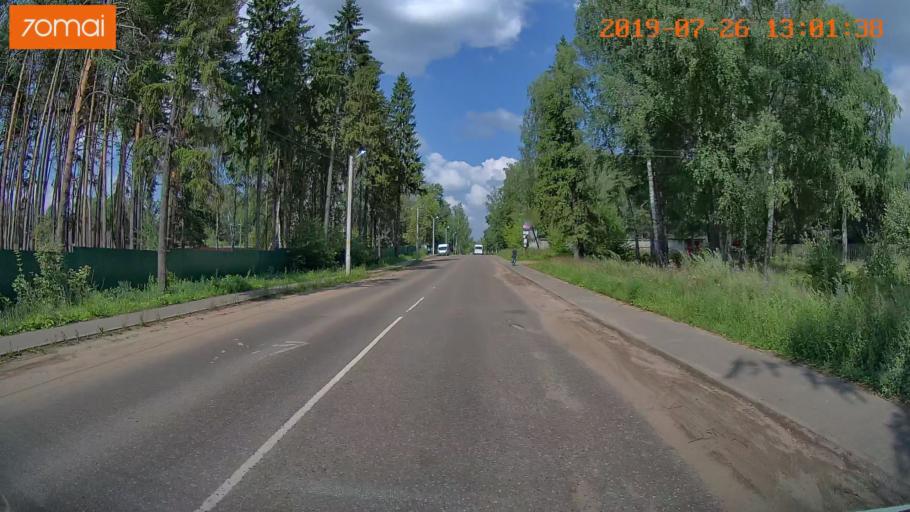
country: RU
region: Ivanovo
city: Bogorodskoye
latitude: 57.0393
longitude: 41.0125
